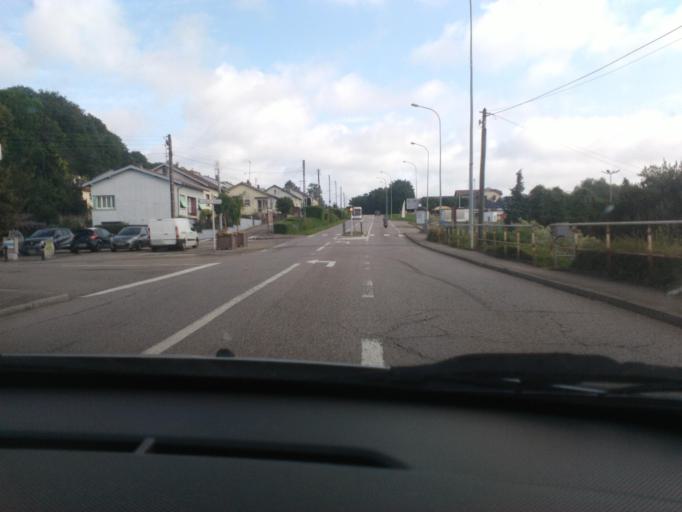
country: FR
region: Lorraine
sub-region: Departement de Meurthe-et-Moselle
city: Pompey
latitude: 48.7783
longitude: 6.1309
